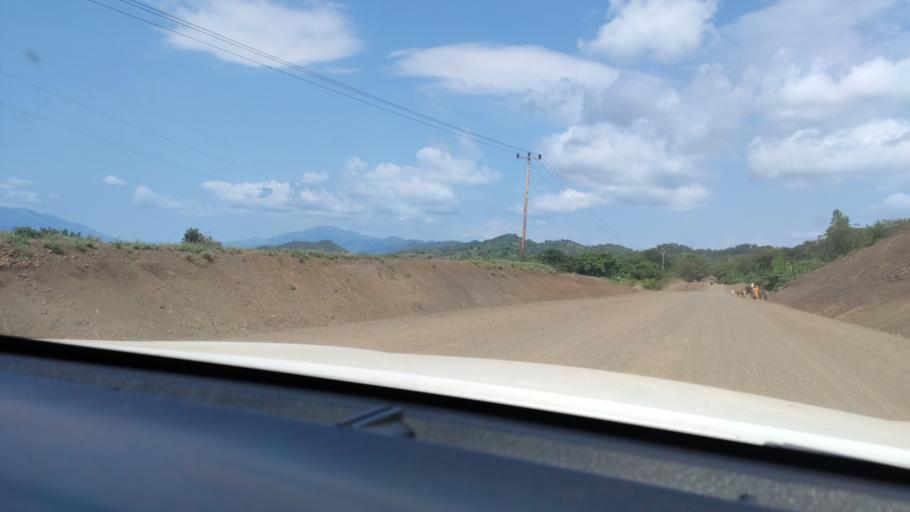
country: ET
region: Southern Nations, Nationalities, and People's Region
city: Felege Neway
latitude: 6.3951
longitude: 37.0764
